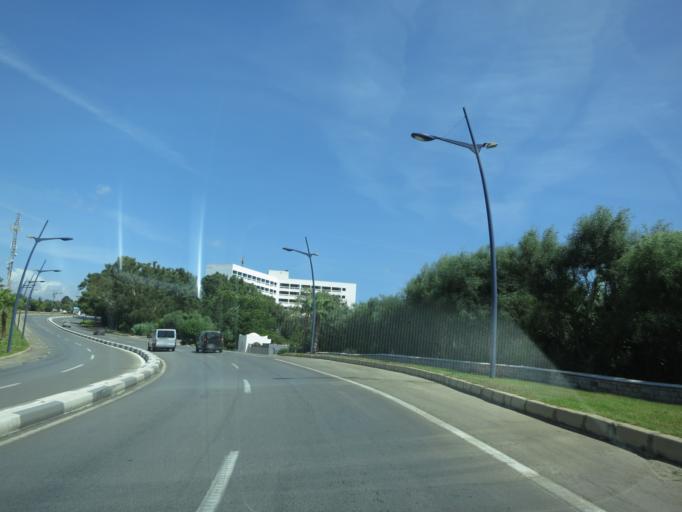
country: ES
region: Ceuta
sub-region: Ceuta
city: Ceuta
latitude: 35.7734
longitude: -5.3484
